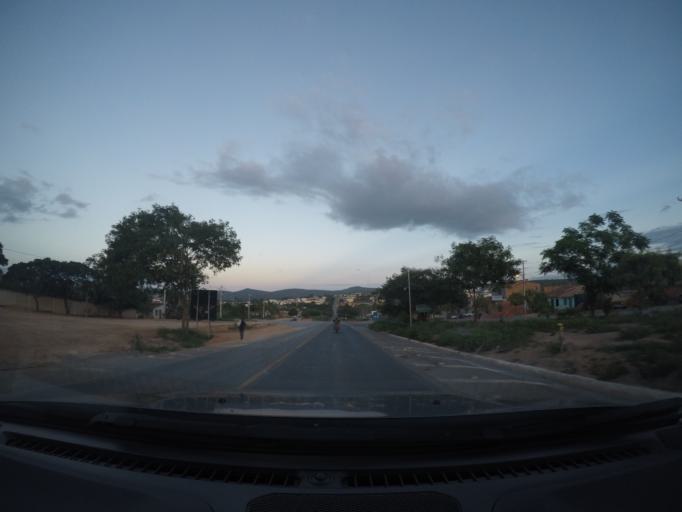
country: BR
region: Bahia
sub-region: Seabra
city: Seabra
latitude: -12.4289
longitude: -41.7808
